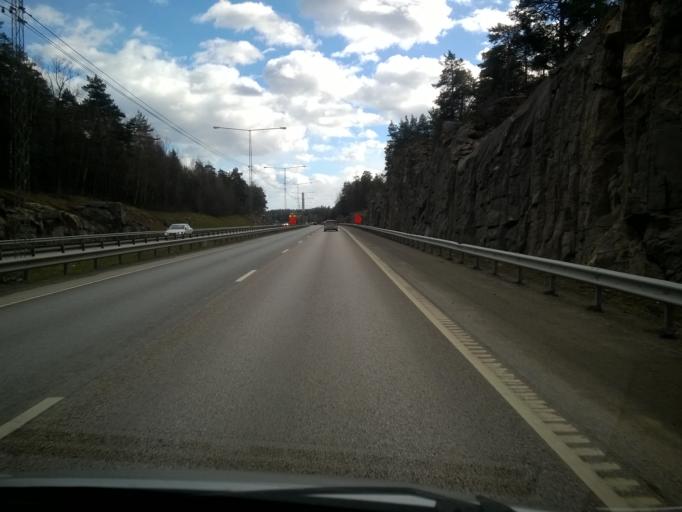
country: SE
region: Stockholm
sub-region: Jarfalla Kommun
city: Jakobsberg
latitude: 59.4377
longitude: 17.8437
